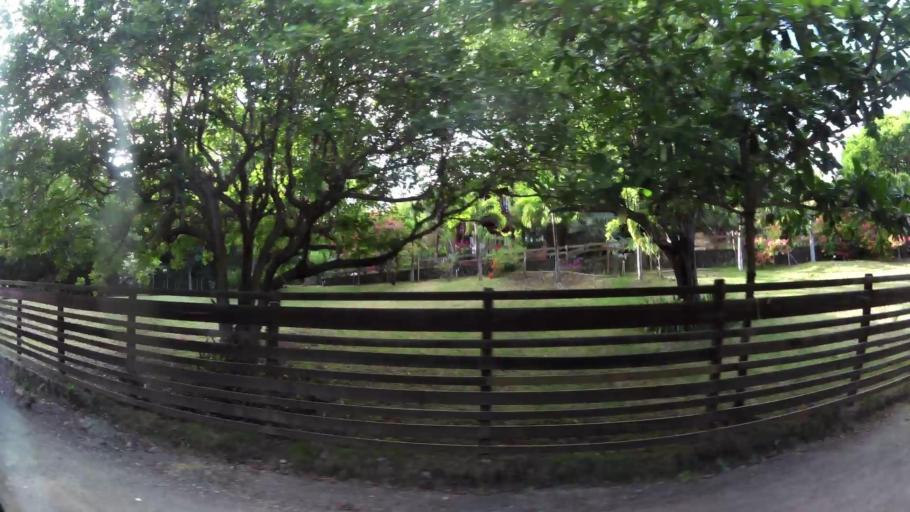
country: LC
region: Gros-Islet
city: Gros Islet
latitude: 14.1001
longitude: -60.9417
